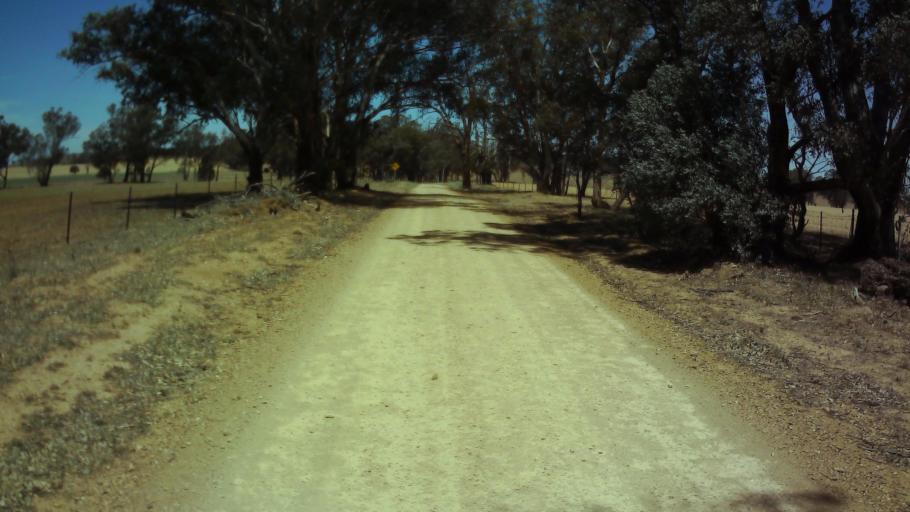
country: AU
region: New South Wales
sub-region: Weddin
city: Grenfell
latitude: -33.9218
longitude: 148.2100
